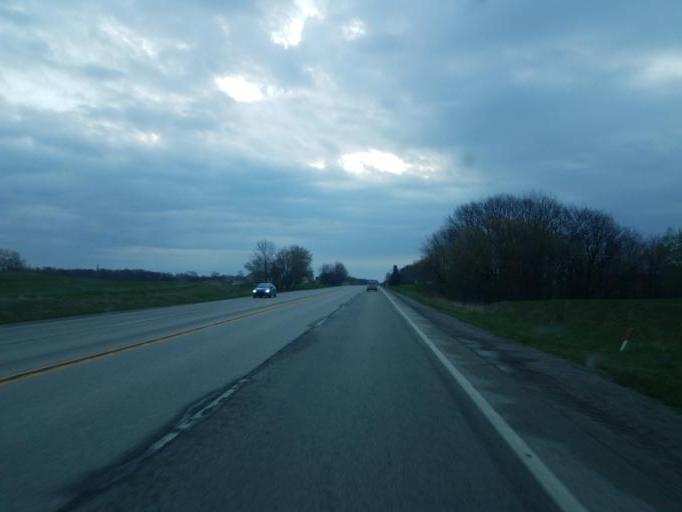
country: US
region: Michigan
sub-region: Isabella County
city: Lake Isabella
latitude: 43.5957
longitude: -85.0298
